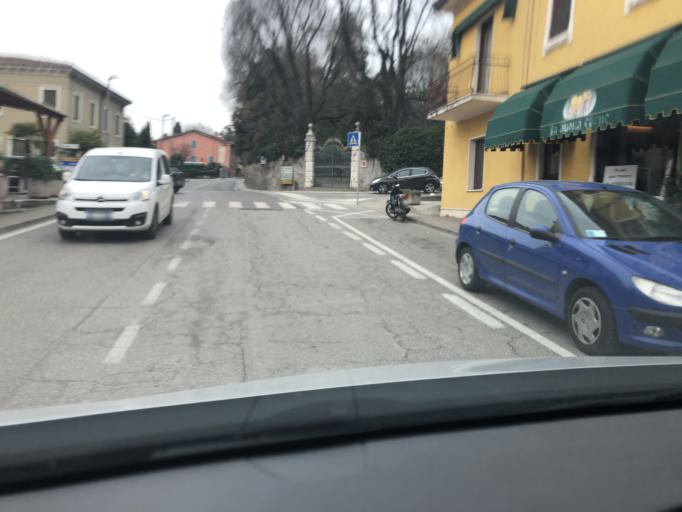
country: IT
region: Veneto
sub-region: Provincia di Verona
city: Sommacampagna
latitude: 45.4054
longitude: 10.8452
